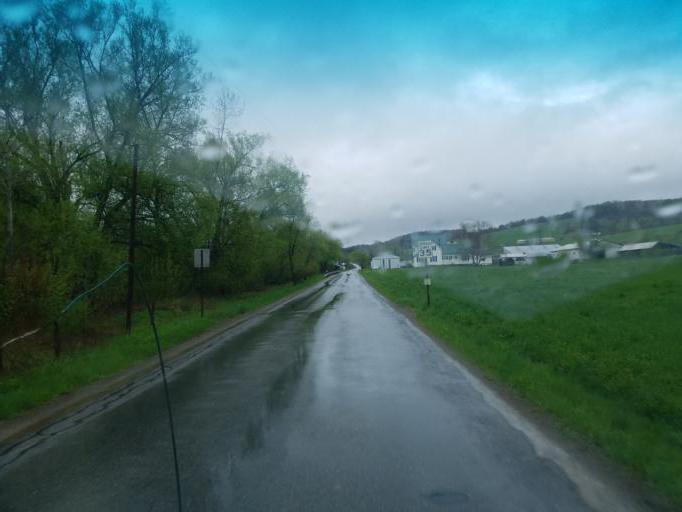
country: US
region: Pennsylvania
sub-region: Tioga County
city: Westfield
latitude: 41.9559
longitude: -77.6477
